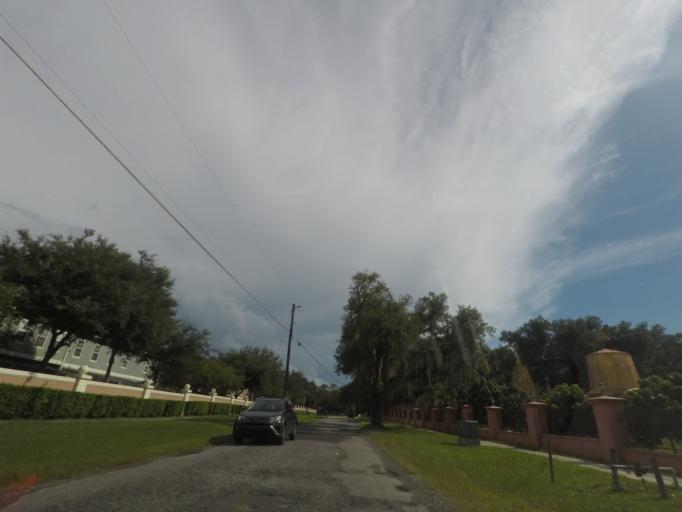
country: US
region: Florida
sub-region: Osceola County
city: Kissimmee
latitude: 28.3177
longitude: -81.4626
